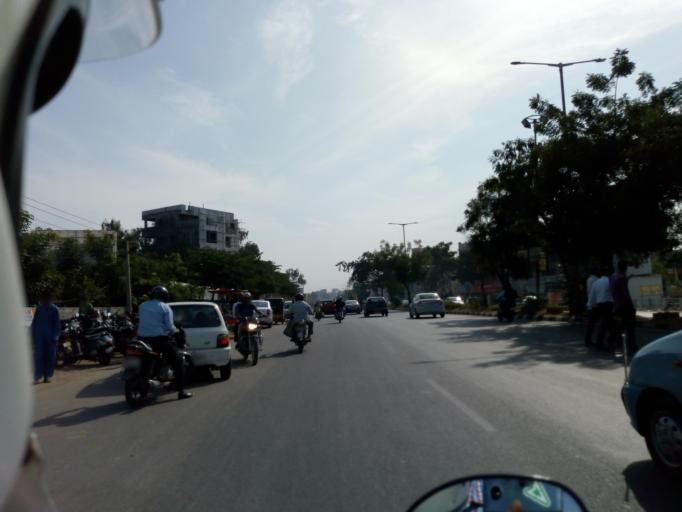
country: IN
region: Telangana
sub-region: Rangareddi
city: Lal Bahadur Nagar
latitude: 17.3700
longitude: 78.5575
